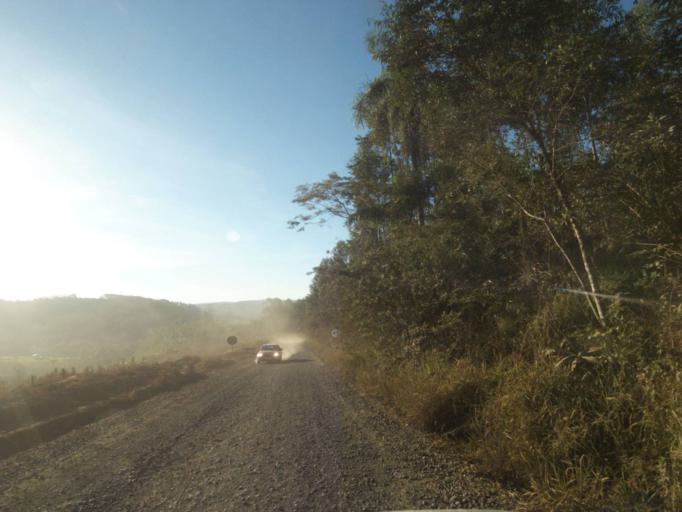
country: BR
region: Parana
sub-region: Telemaco Borba
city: Telemaco Borba
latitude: -24.4204
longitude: -50.5900
